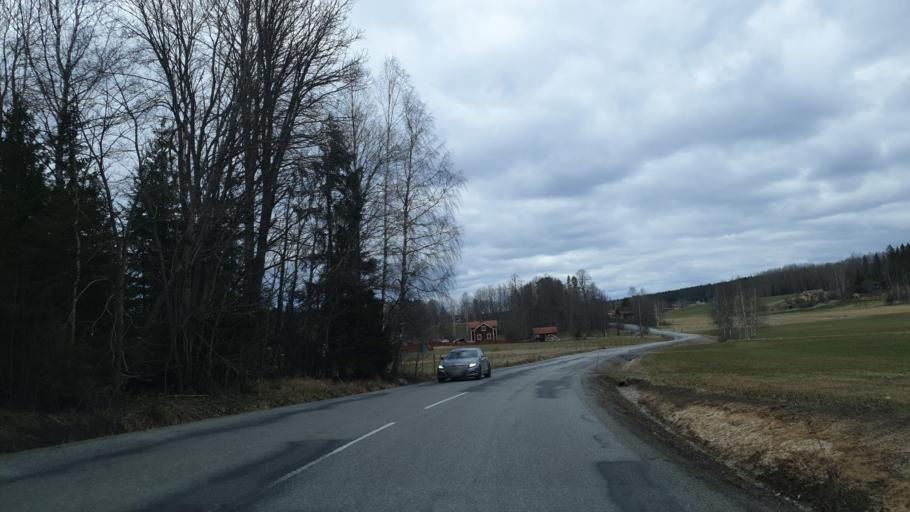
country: SE
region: OErebro
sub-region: Nora Kommun
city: Nora
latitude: 59.5496
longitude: 15.0294
